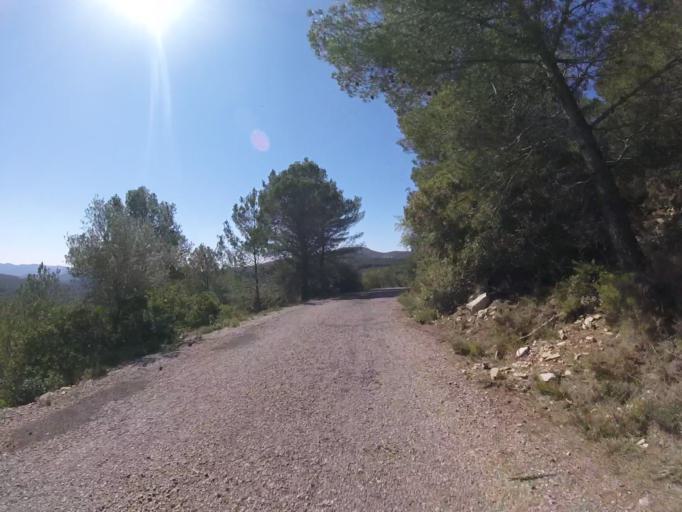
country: ES
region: Valencia
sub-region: Provincia de Castello
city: Cervera del Maestre
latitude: 40.4083
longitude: 0.1987
